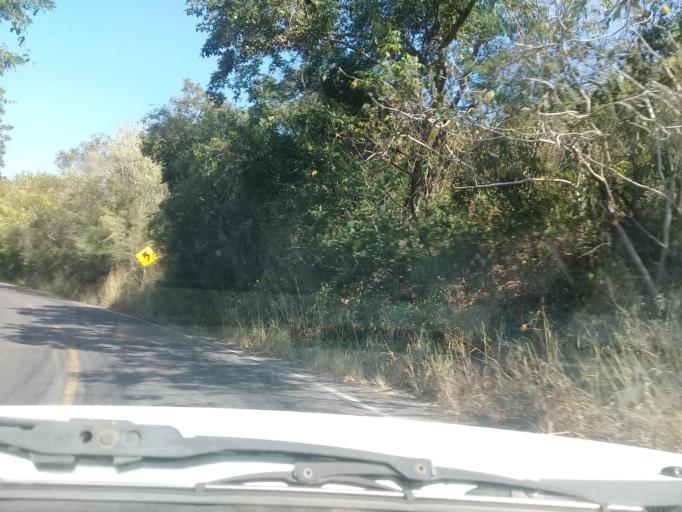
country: MX
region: Veracruz
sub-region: Emiliano Zapata
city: Plan del Rio
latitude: 19.4143
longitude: -96.6131
